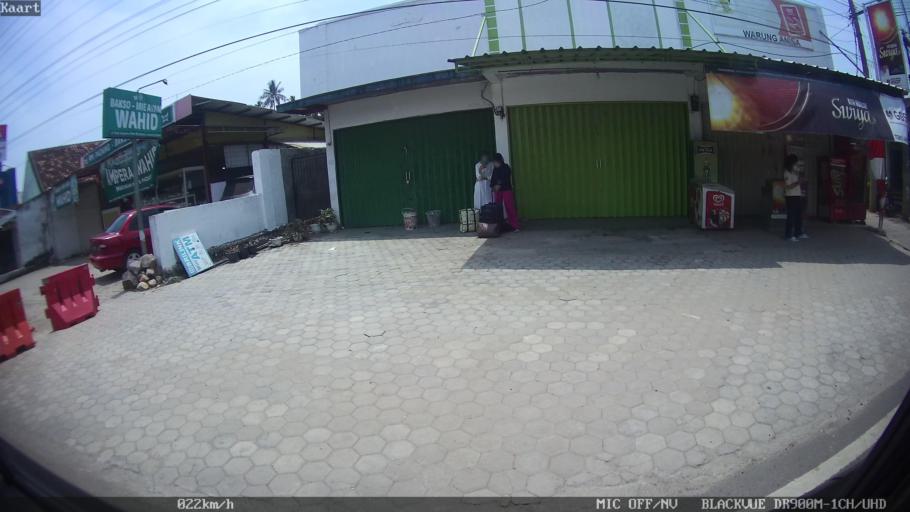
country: ID
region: Lampung
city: Kedaton
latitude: -5.3612
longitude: 105.2251
